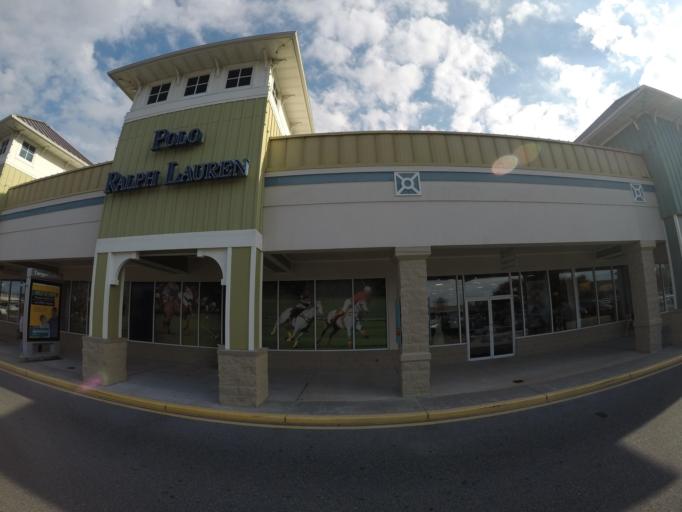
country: US
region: Delaware
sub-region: Sussex County
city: Lewes
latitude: 38.7337
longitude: -75.1398
